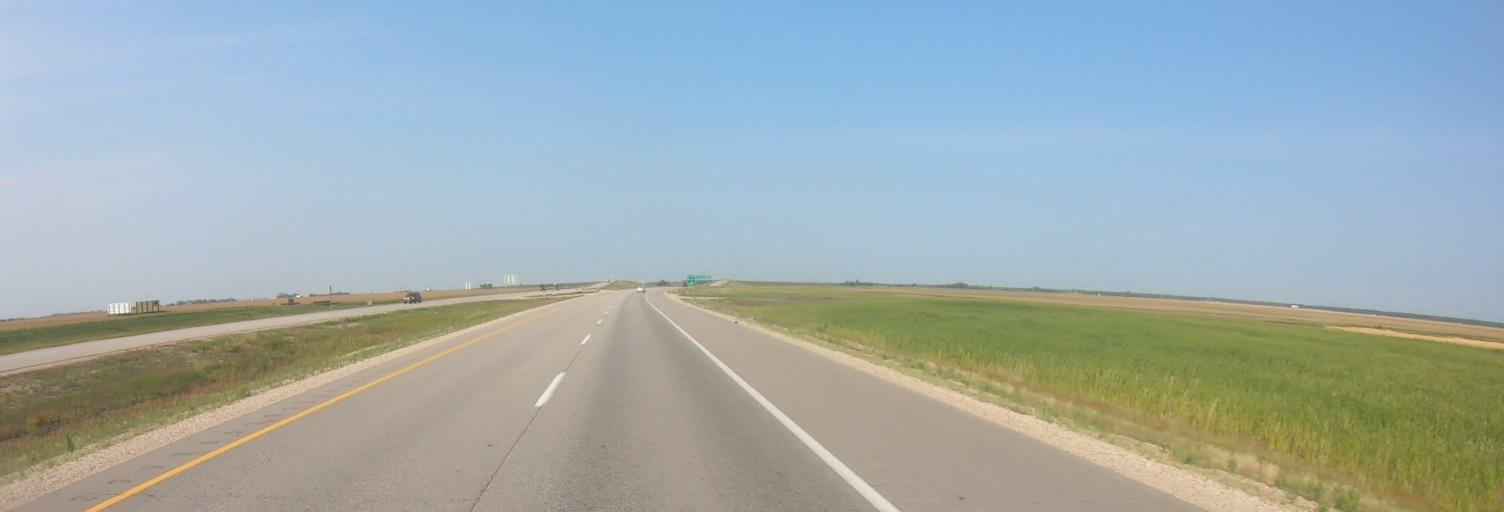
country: CA
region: Manitoba
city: Steinbach
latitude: 49.6915
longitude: -96.6534
